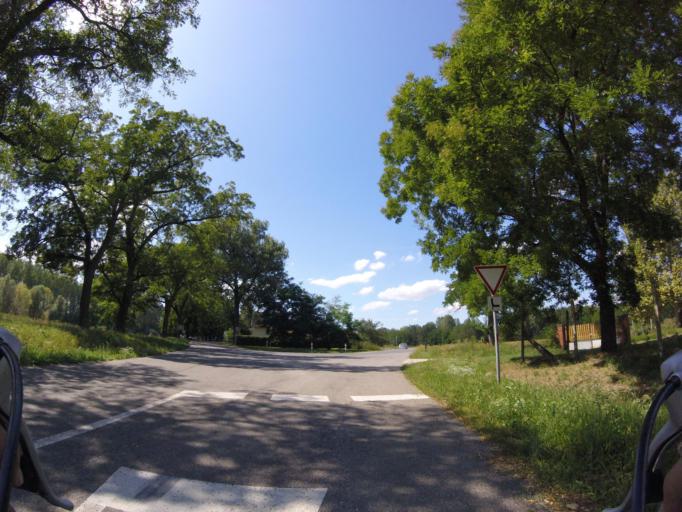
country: HU
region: Gyor-Moson-Sopron
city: Szany
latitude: 47.4380
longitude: 17.3322
